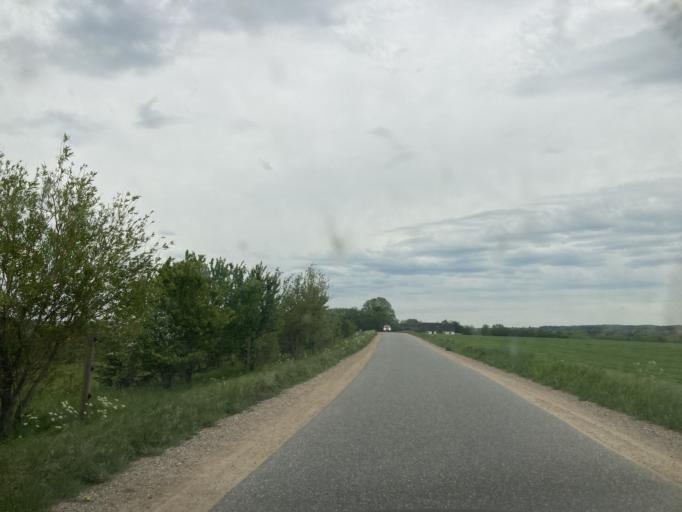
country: DK
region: Zealand
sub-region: Roskilde Kommune
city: Svogerslev
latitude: 55.6397
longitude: 11.9819
